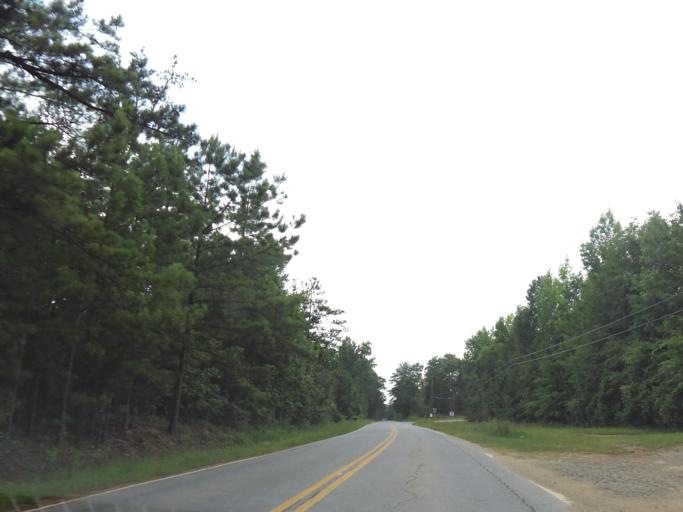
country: US
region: Georgia
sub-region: Bibb County
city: West Point
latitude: 32.8090
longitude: -83.8374
